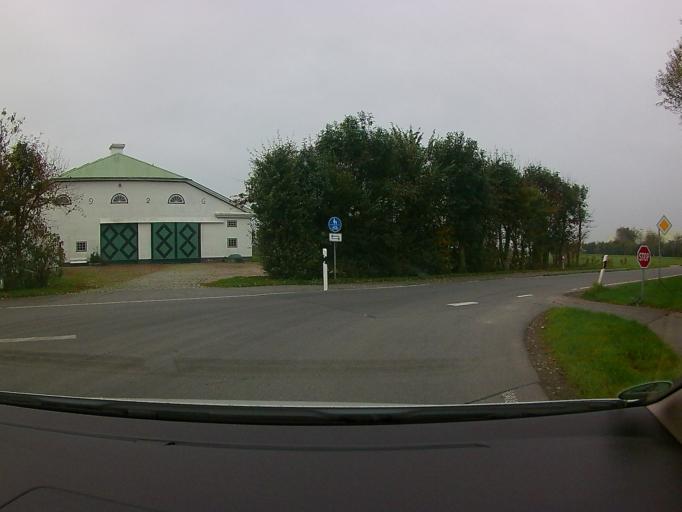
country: DE
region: Schleswig-Holstein
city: Reussenkoge
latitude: 54.6204
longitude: 8.8831
